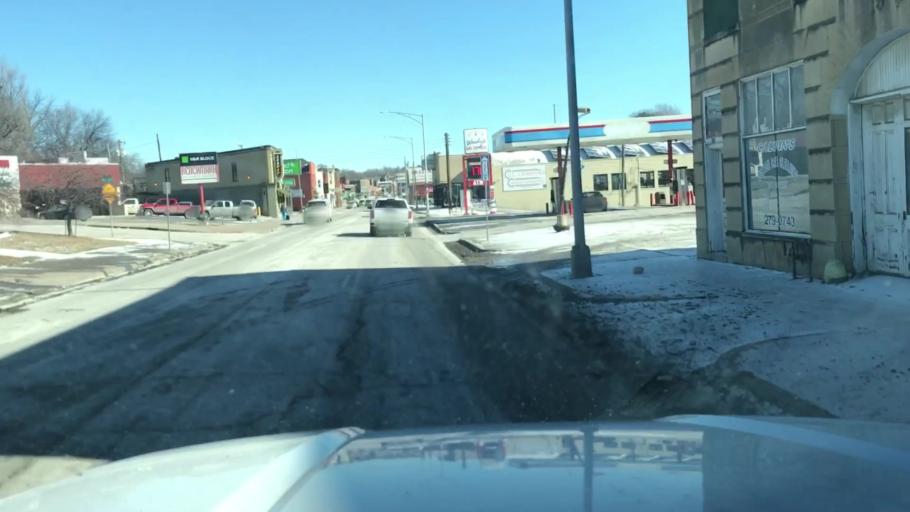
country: US
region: Missouri
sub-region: Buchanan County
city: Saint Joseph
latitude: 39.7709
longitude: -94.8434
